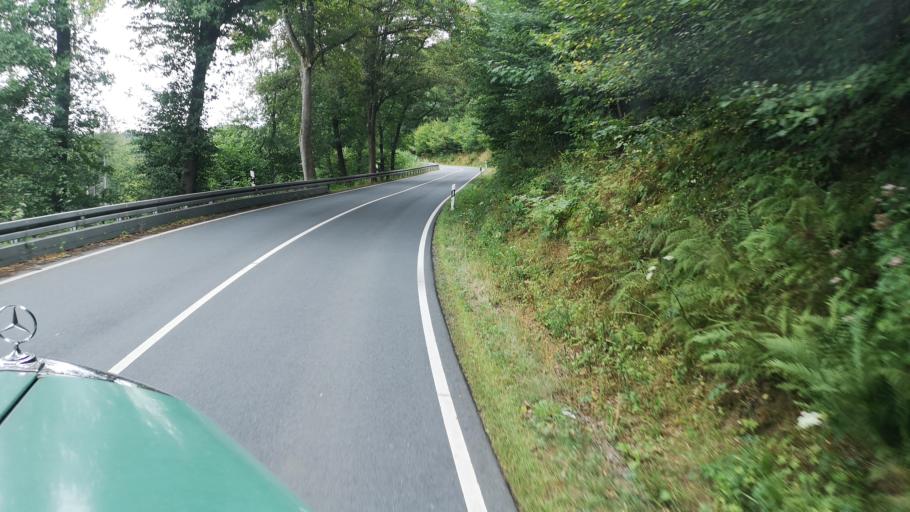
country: DE
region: North Rhine-Westphalia
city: Burscheid
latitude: 51.0705
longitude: 7.1435
